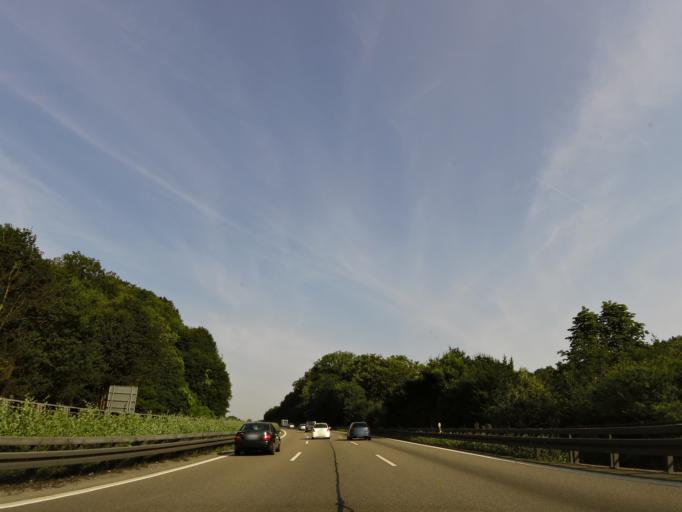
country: DE
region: Baden-Wuerttemberg
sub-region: Karlsruhe Region
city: Kieselbronn
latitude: 48.9233
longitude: 8.7548
